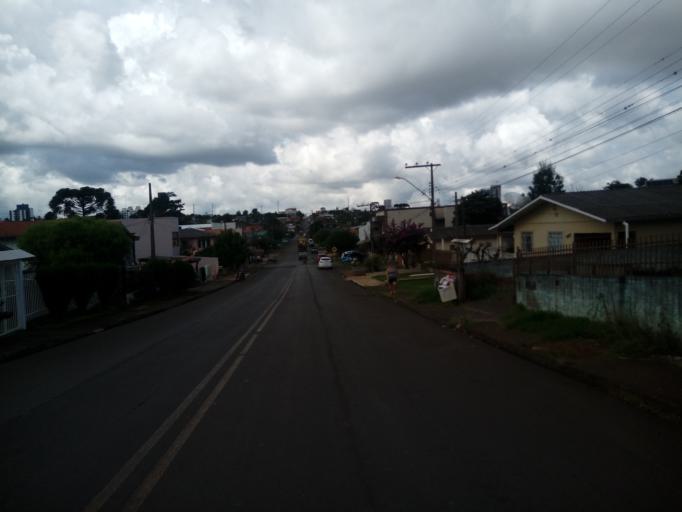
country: BR
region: Santa Catarina
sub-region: Chapeco
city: Chapeco
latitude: -27.0762
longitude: -52.6100
